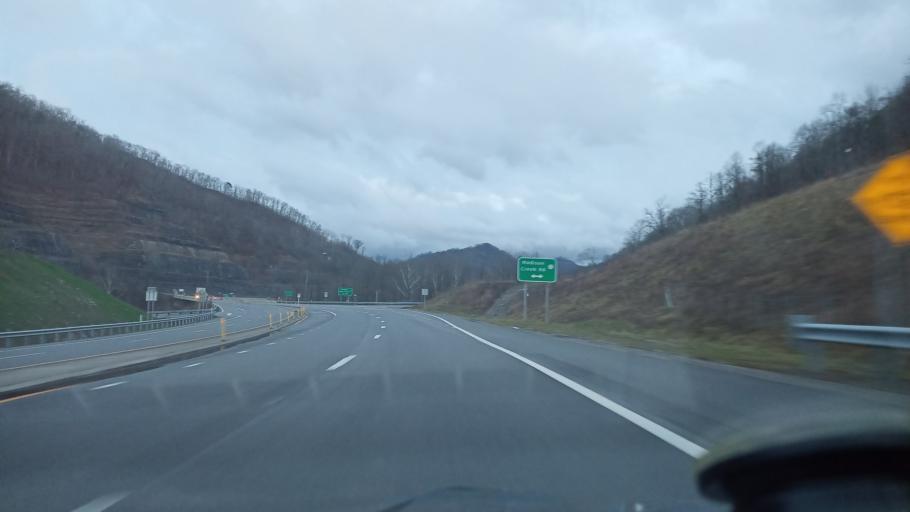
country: US
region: West Virginia
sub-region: Logan County
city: Logan
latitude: 37.7801
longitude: -81.9407
